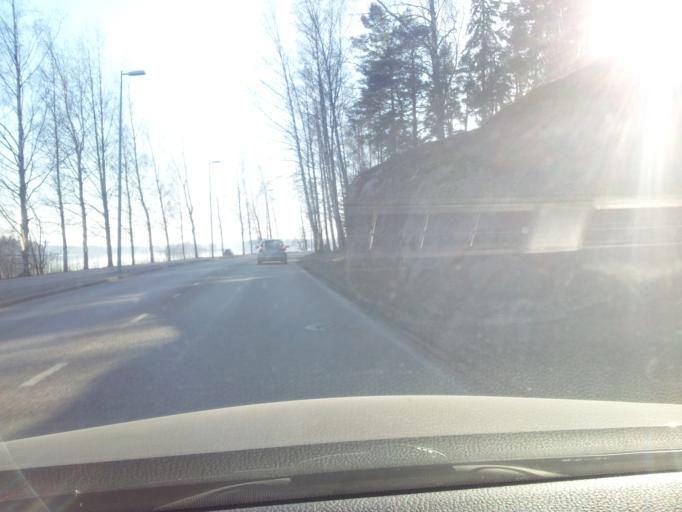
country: FI
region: Uusimaa
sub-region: Helsinki
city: Teekkarikylae
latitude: 60.1902
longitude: 24.8772
